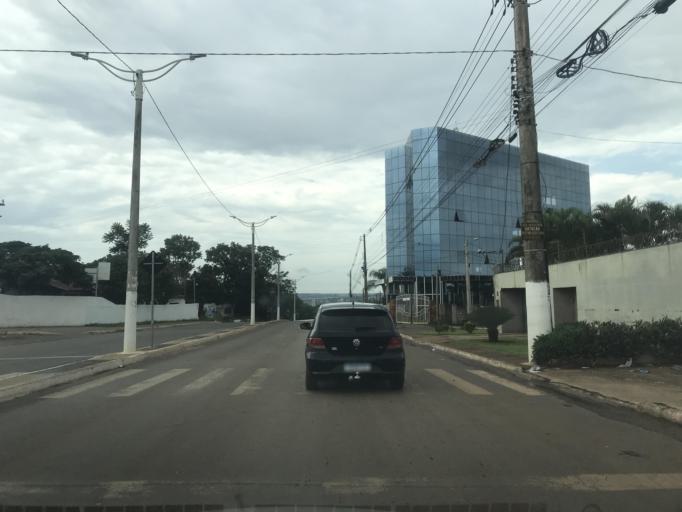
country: BR
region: Goias
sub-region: Luziania
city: Luziania
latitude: -16.2395
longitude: -47.9432
